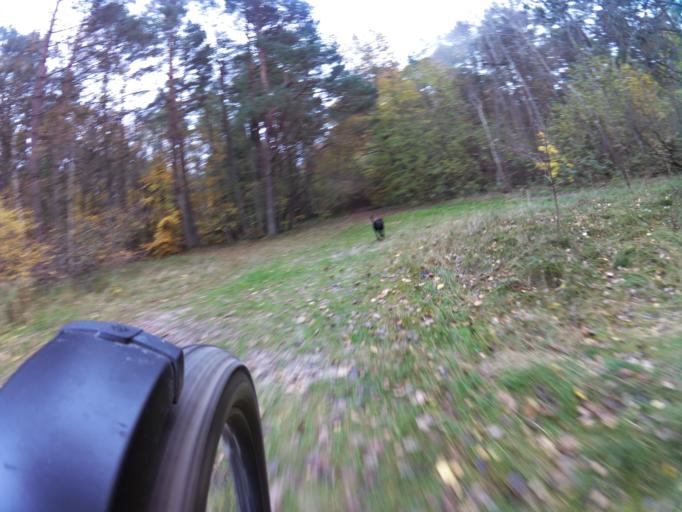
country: PL
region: Pomeranian Voivodeship
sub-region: Powiat pucki
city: Krokowa
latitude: 54.8307
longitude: 18.1436
